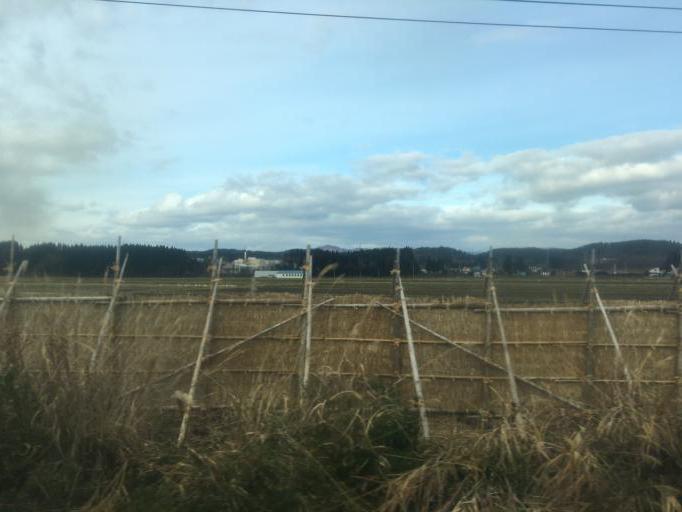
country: JP
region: Akita
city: Takanosu
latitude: 40.2500
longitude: 140.3967
